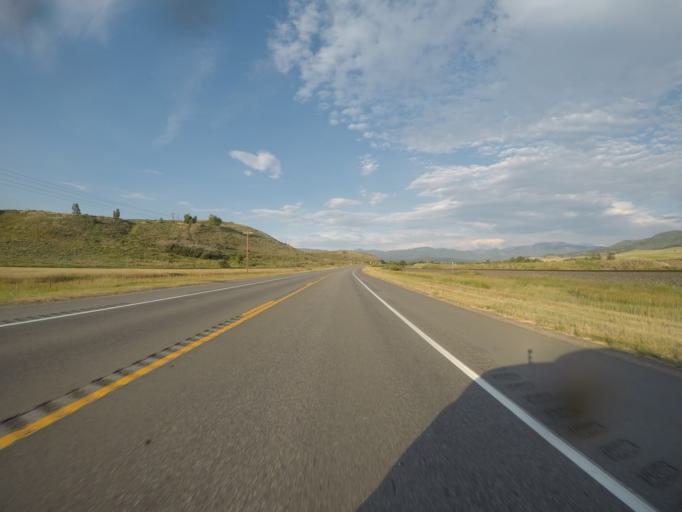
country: US
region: Colorado
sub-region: Routt County
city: Steamboat Springs
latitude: 40.4998
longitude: -106.9327
